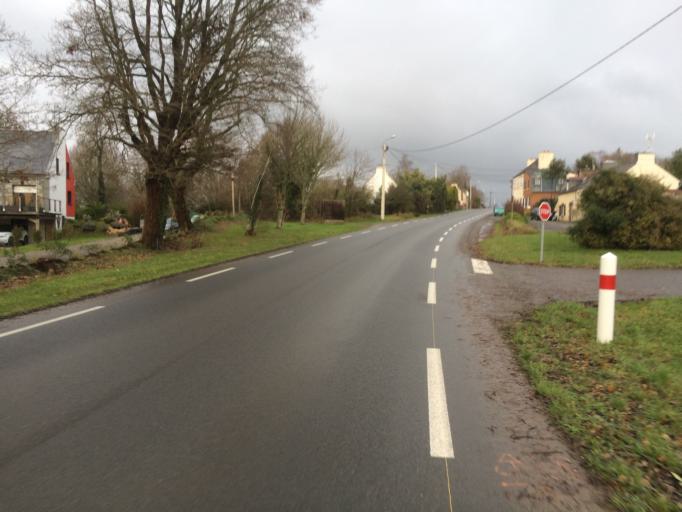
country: FR
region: Brittany
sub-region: Departement du Finistere
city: Logonna-Daoulas
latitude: 48.3303
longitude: -4.2929
